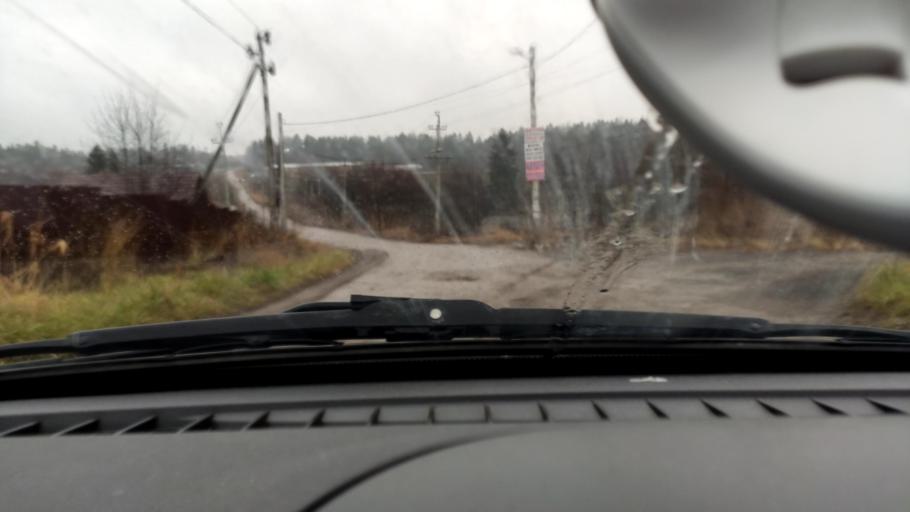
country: RU
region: Perm
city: Perm
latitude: 58.0364
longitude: 56.4089
